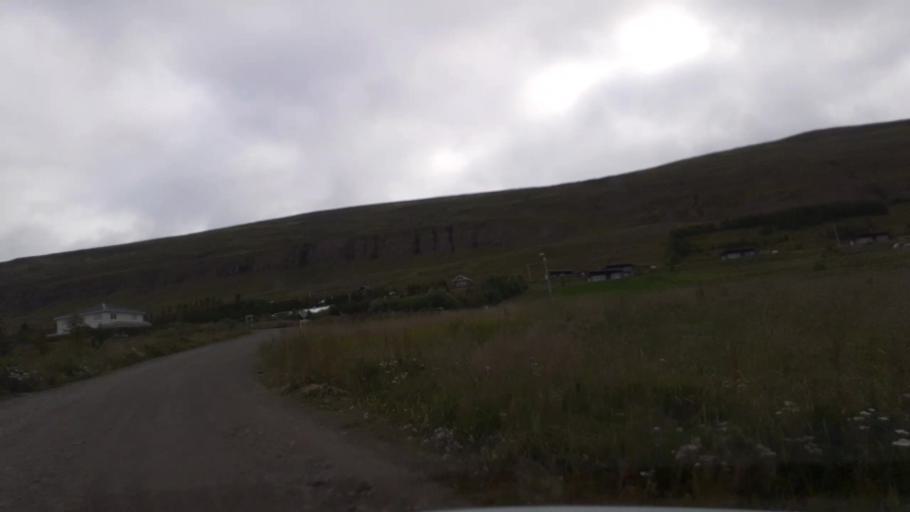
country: IS
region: Northeast
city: Akureyri
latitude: 65.6787
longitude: -18.0392
